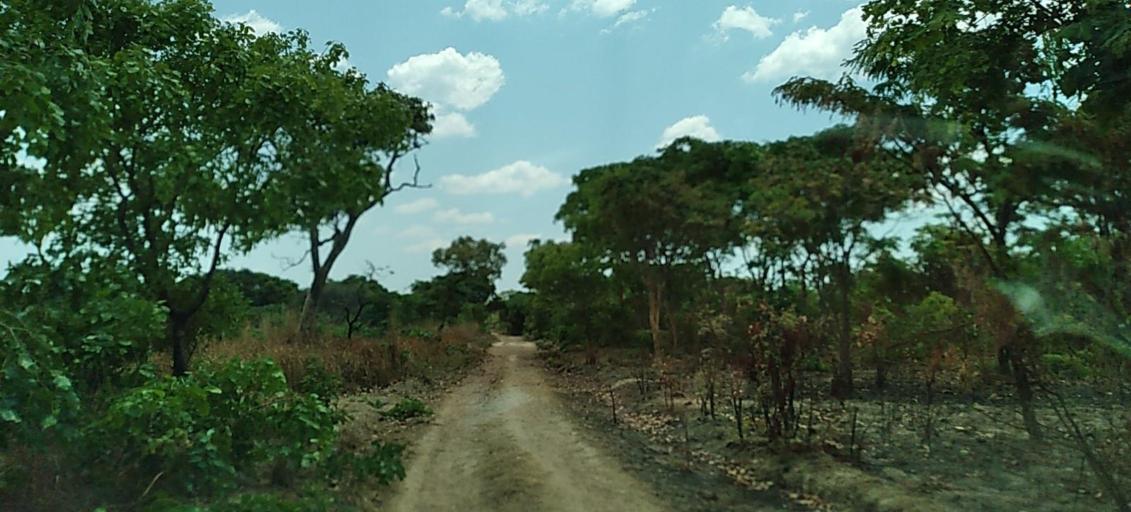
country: ZM
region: Copperbelt
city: Chililabombwe
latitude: -12.4566
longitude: 27.6716
